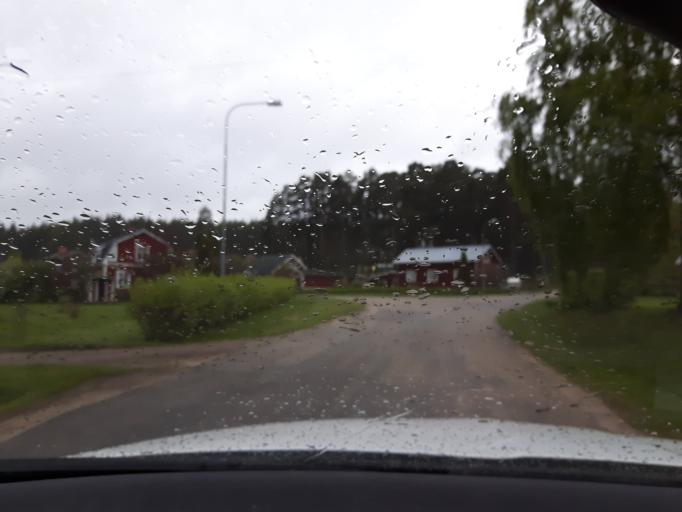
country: SE
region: Gaevleborg
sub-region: Ljusdals Kommun
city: Farila
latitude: 62.0276
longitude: 15.9257
